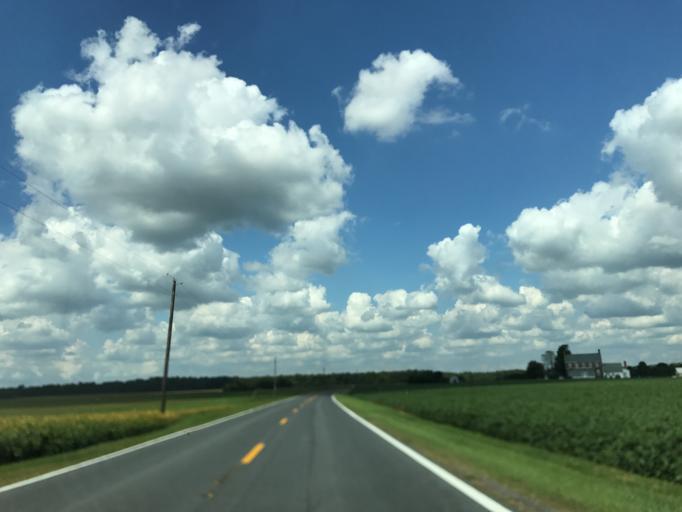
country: US
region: Maryland
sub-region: Caroline County
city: Ridgely
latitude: 39.0432
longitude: -75.9143
